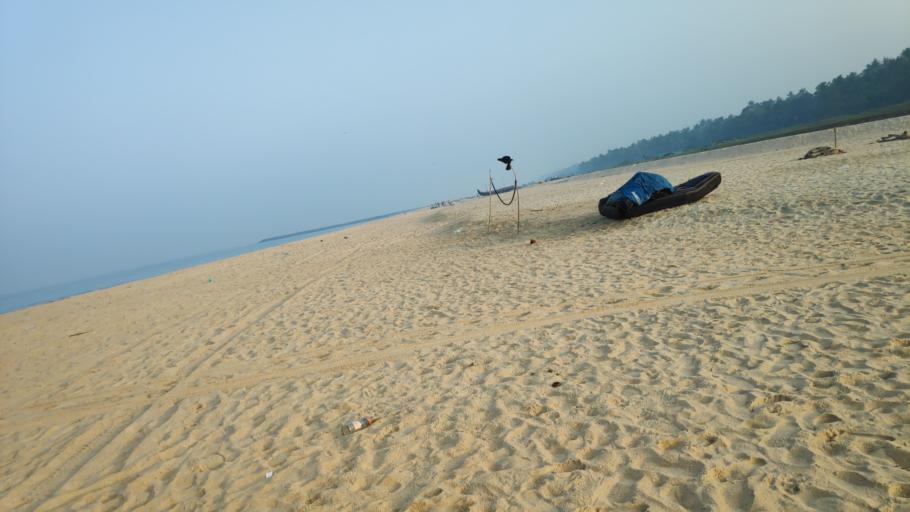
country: IN
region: Kerala
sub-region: Alappuzha
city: Vayalar
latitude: 9.6625
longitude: 76.2915
